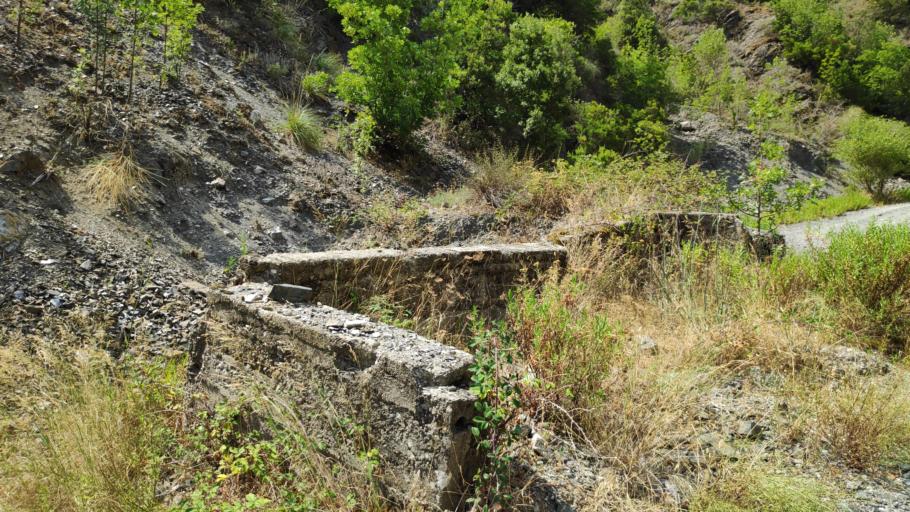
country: IT
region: Calabria
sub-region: Provincia di Reggio Calabria
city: Bivongi
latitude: 38.4929
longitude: 16.4516
